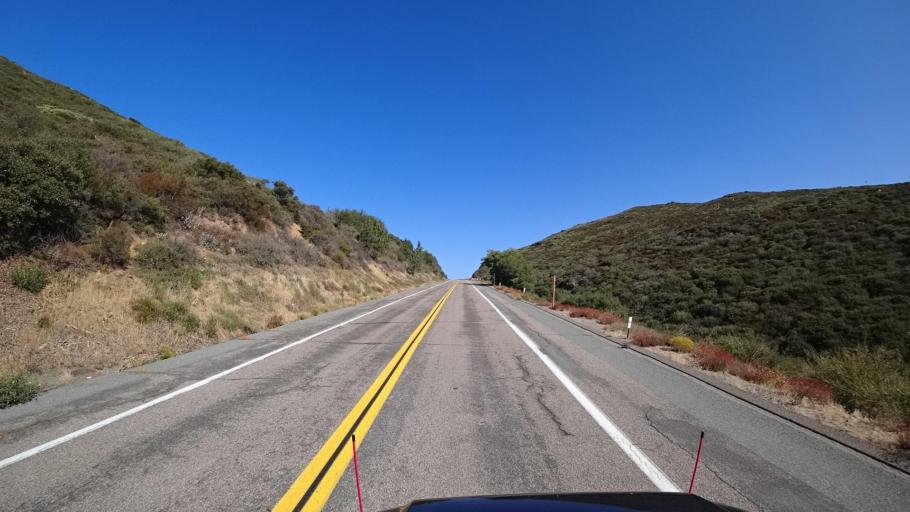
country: US
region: California
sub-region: San Diego County
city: Pine Valley
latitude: 32.9265
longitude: -116.4843
